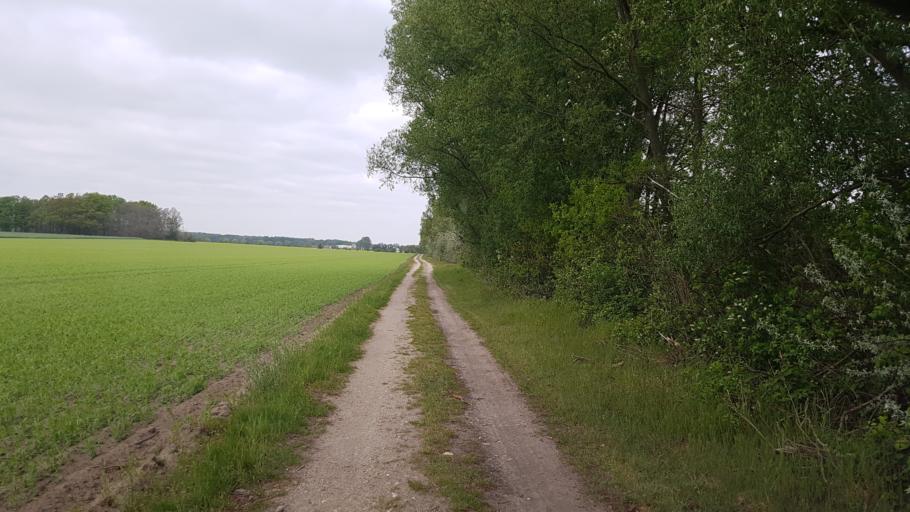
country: DE
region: Brandenburg
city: Sonnewalde
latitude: 51.6806
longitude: 13.6351
